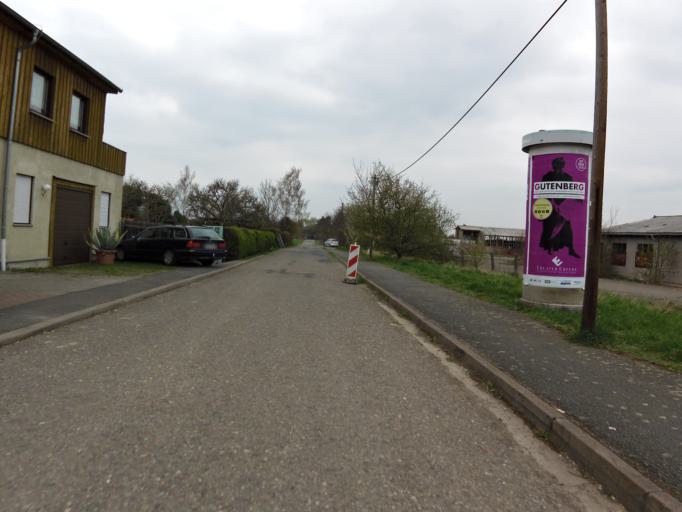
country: DE
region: Thuringia
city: Gotha
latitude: 50.9566
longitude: 10.6976
